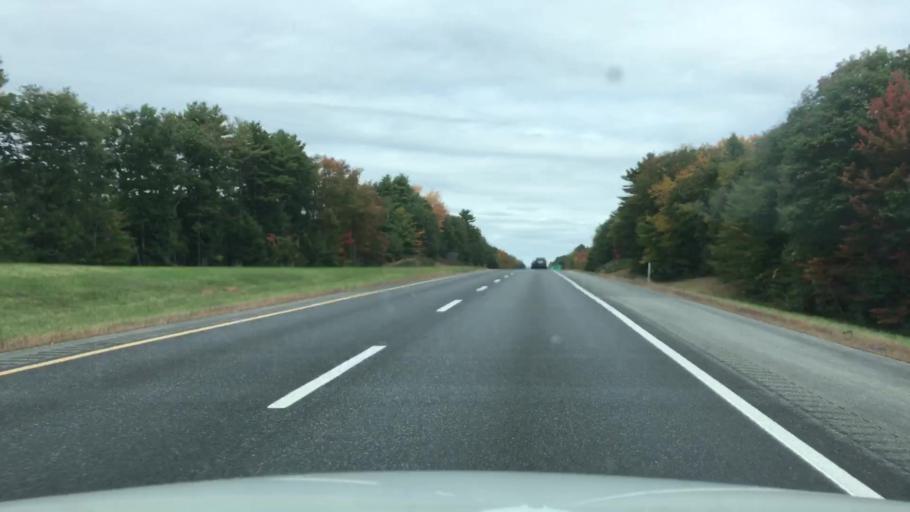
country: US
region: Maine
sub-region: Kennebec County
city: Gardiner
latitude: 44.1688
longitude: -69.8341
